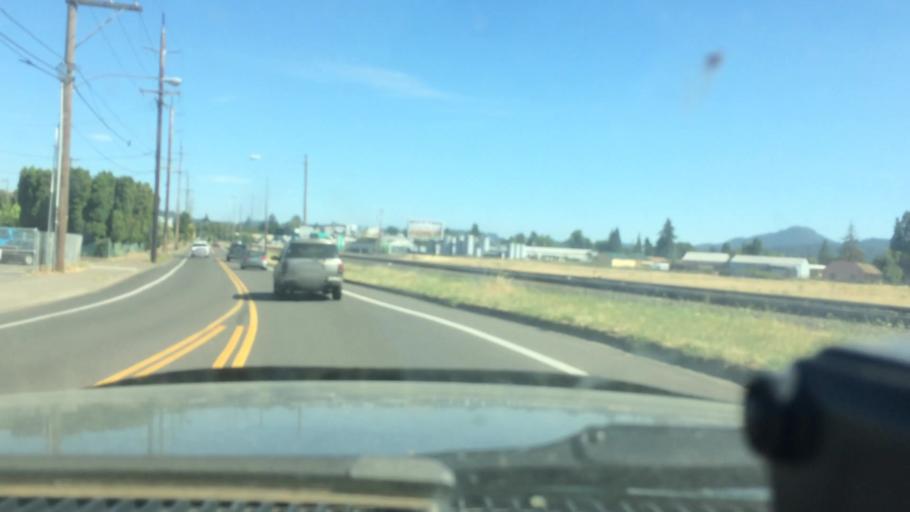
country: US
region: Oregon
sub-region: Lane County
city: Eugene
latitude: 44.0623
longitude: -123.1164
